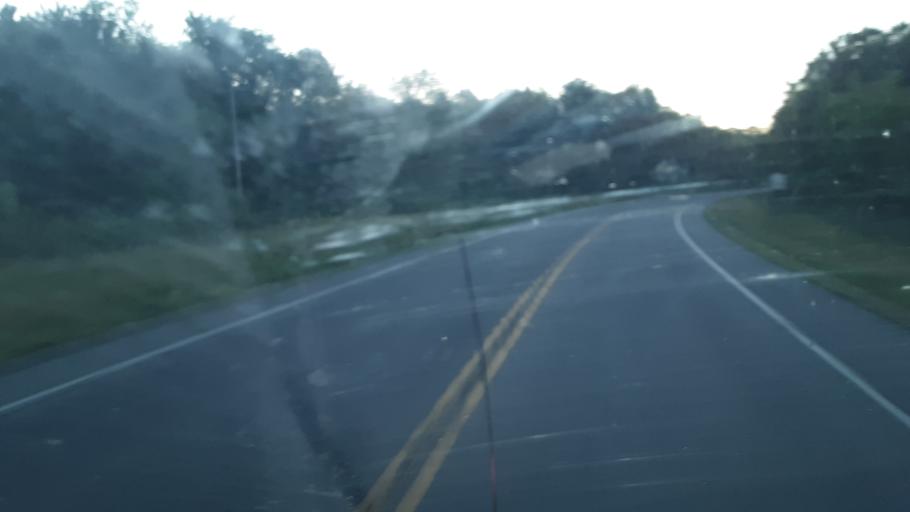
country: US
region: New York
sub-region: Saratoga County
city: Ballston Spa
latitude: 42.9946
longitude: -73.9212
